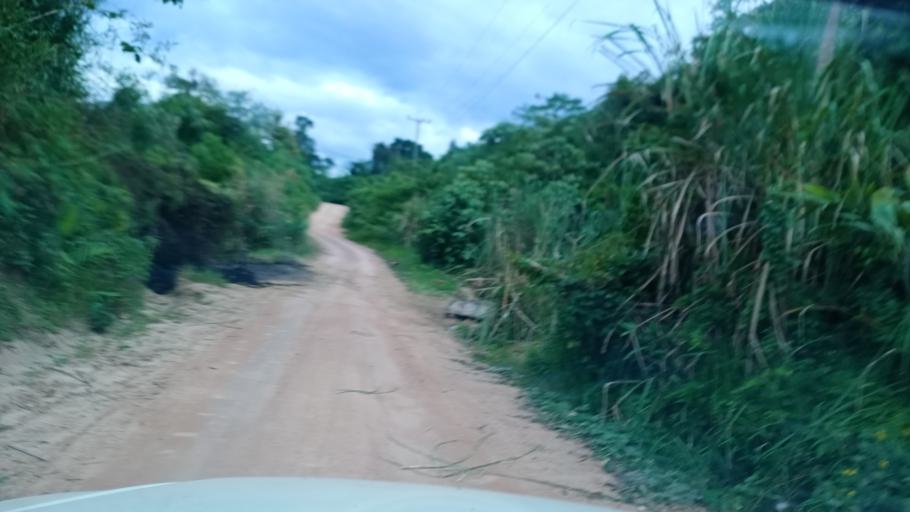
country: TH
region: Changwat Bueng Kan
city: Pak Khat
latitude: 18.7229
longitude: 103.2801
